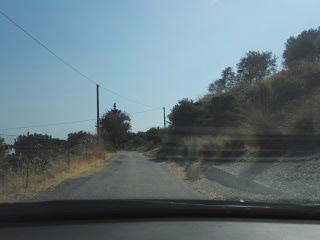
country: IT
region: Calabria
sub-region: Provincia di Reggio Calabria
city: Stilo
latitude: 38.4514
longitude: 16.4609
